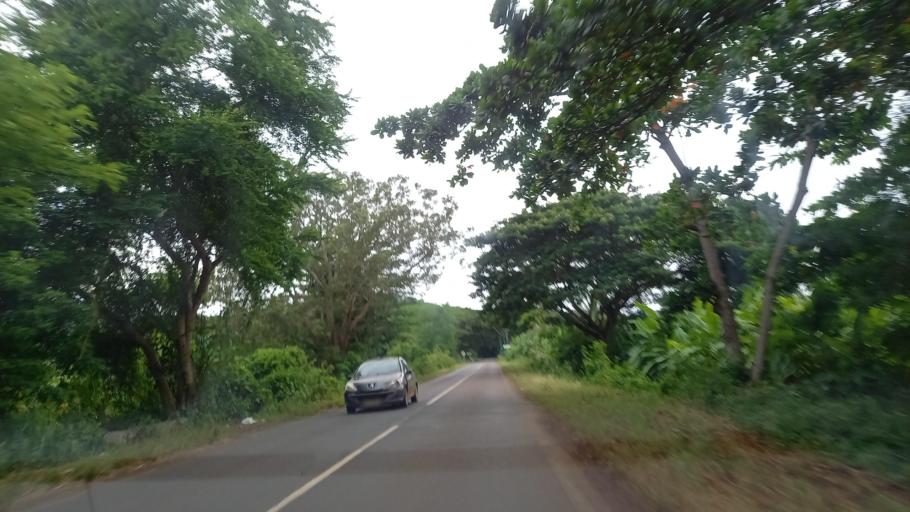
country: YT
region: Chirongui
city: Chirongui
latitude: -12.9146
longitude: 45.1589
